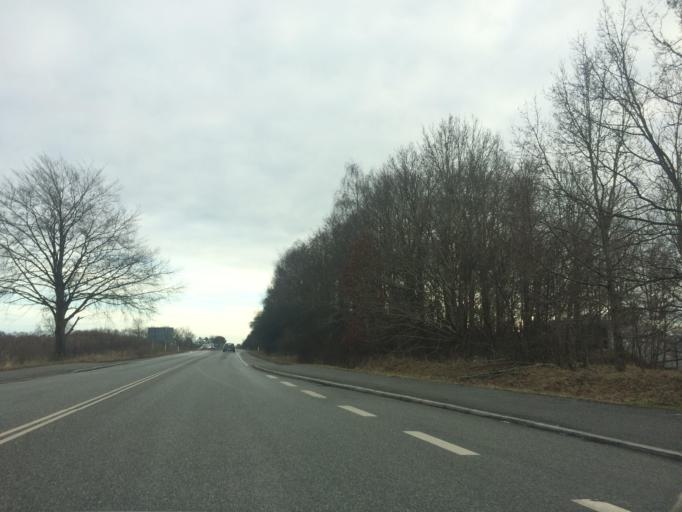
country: DK
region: Capital Region
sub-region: Fredensborg Kommune
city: Fredensborg
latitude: 55.9646
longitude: 12.4068
